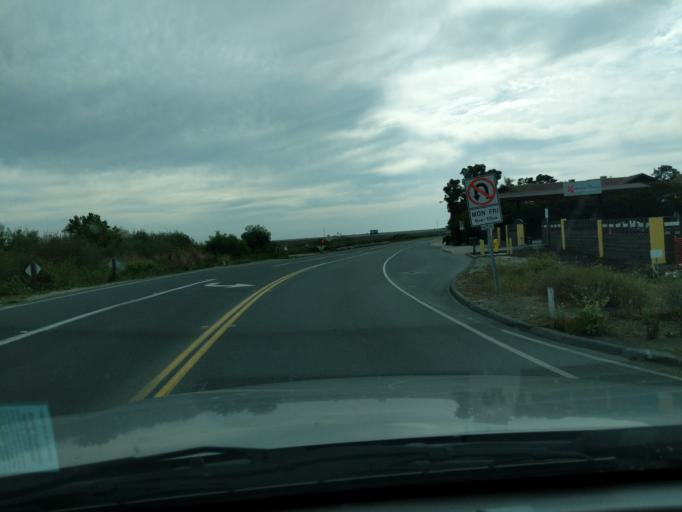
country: US
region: California
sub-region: San Diego County
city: Solana Beach
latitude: 33.0098
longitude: -117.2664
